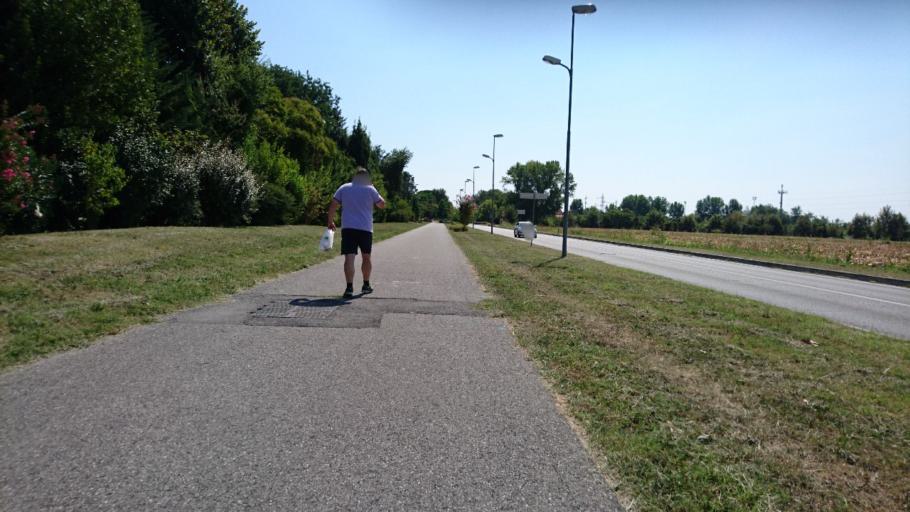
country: IT
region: Veneto
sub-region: Provincia di Padova
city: Mandriola-Sant'Agostino
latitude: 45.3780
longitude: 11.8659
